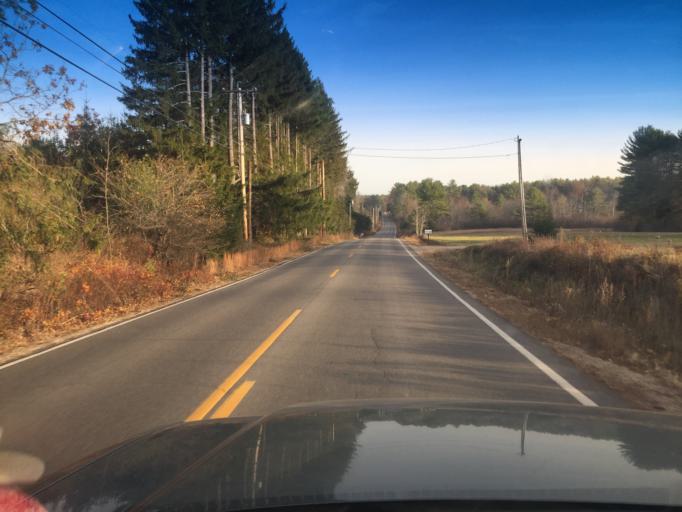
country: US
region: Maine
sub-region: York County
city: Eliot
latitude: 43.1846
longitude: -70.7418
